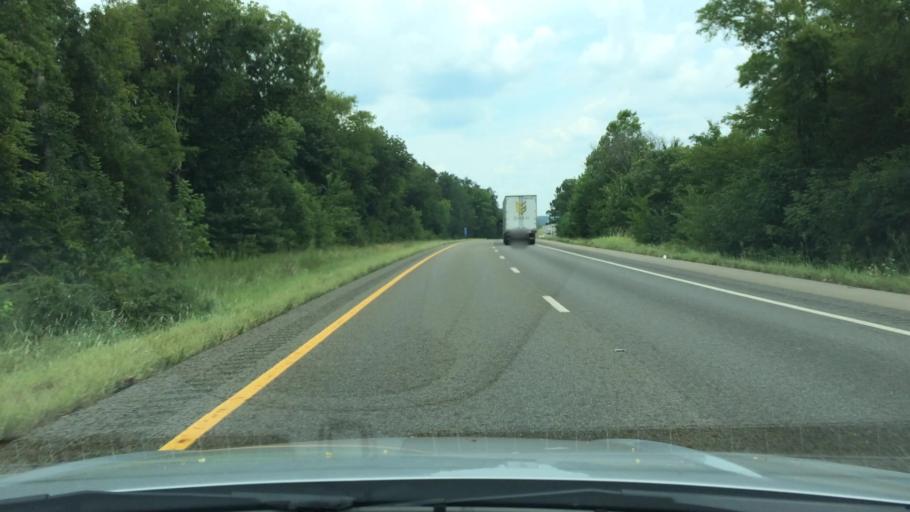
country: US
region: Tennessee
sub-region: Maury County
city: Columbia
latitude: 35.5509
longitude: -86.9077
